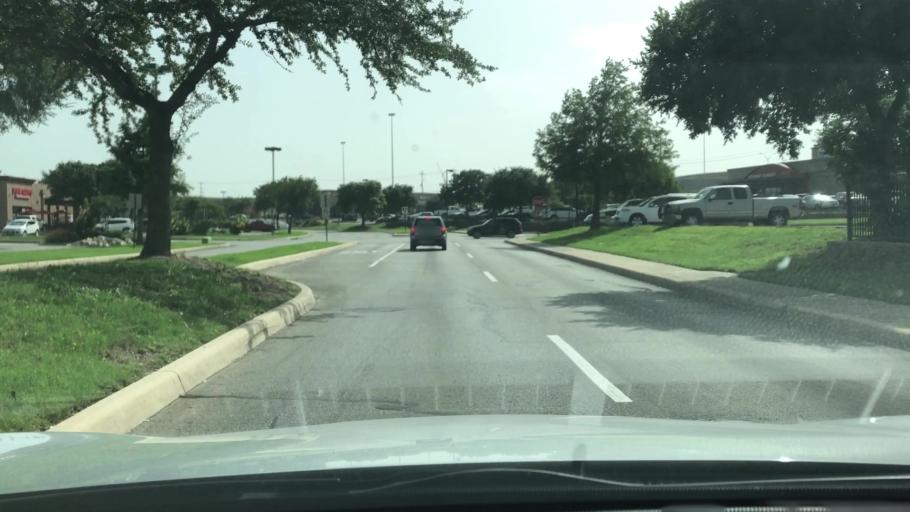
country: US
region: Texas
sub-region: Bexar County
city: Live Oak
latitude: 29.5701
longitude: -98.3281
